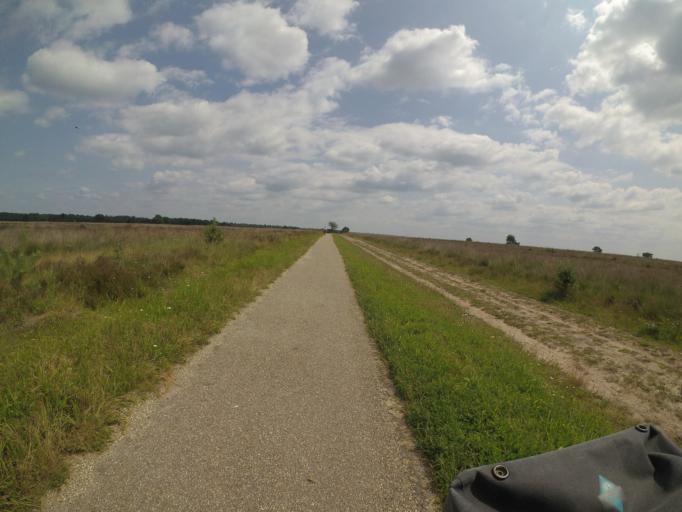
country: NL
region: Gelderland
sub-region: Gemeente Barneveld
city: Garderen
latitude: 52.2668
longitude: 5.7247
